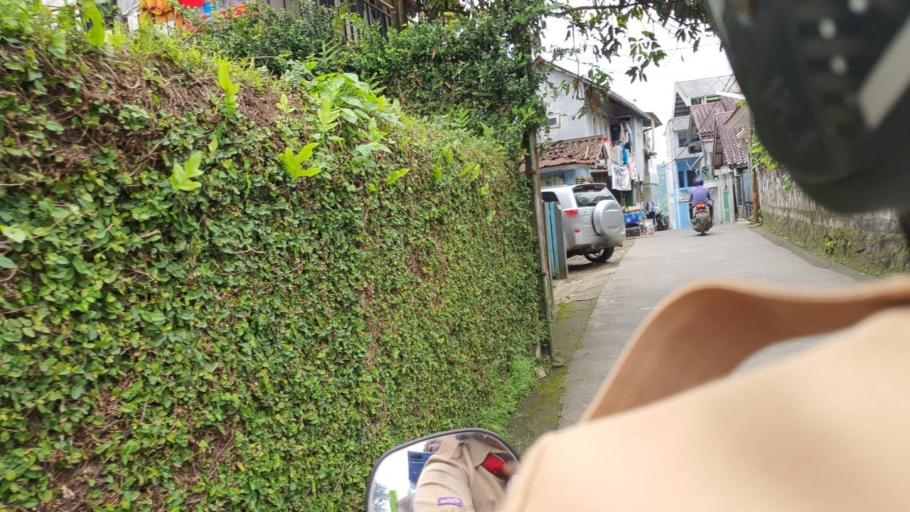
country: ID
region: West Java
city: Caringin
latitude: -6.6509
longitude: 106.8868
